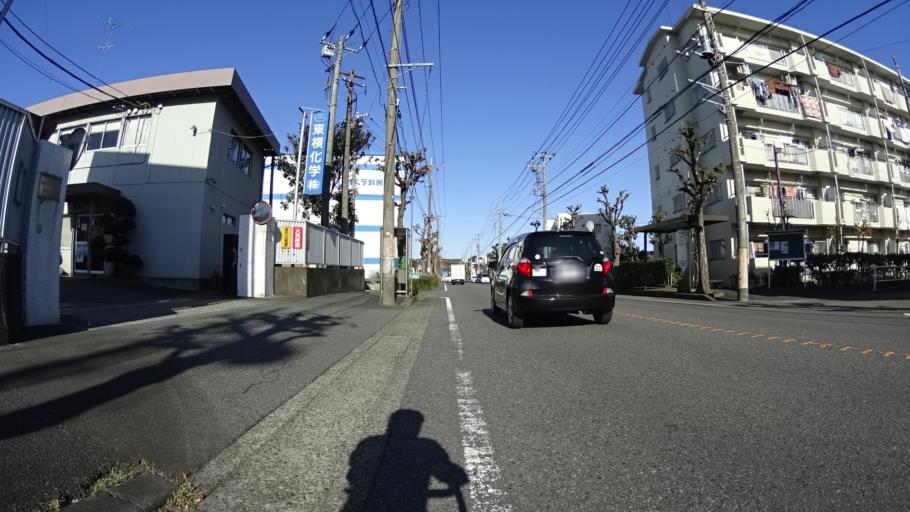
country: JP
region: Tokyo
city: Hachioji
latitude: 35.5894
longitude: 139.3667
